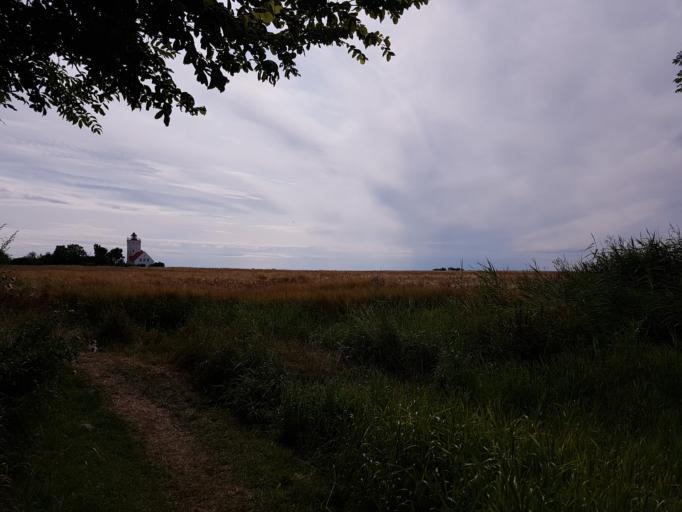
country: DK
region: Zealand
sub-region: Guldborgsund Kommune
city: Nykobing Falster
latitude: 54.5660
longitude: 11.9672
